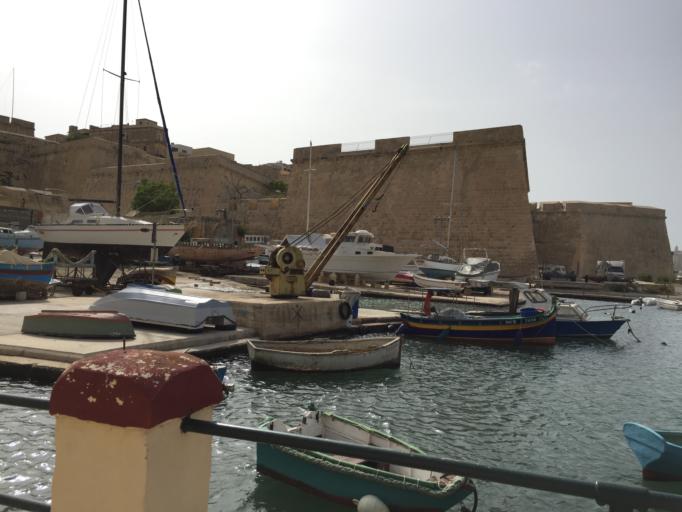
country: MT
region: Bormla
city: Cospicua
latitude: 35.8877
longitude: 14.5262
